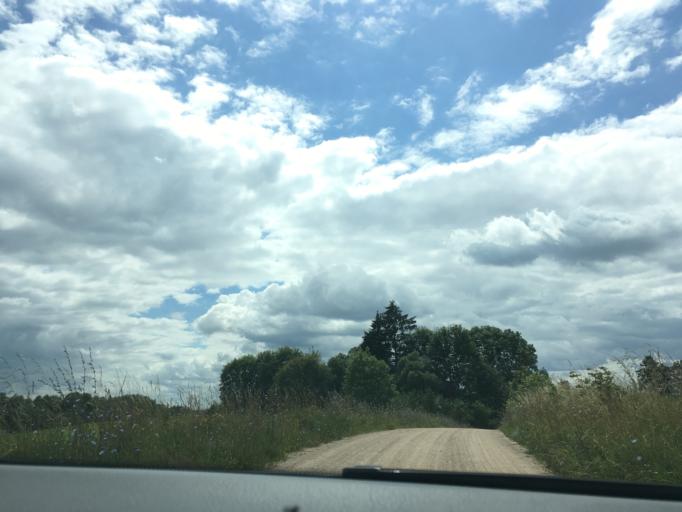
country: PL
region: Podlasie
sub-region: Powiat sejnenski
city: Krasnopol
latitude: 54.0952
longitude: 23.2711
